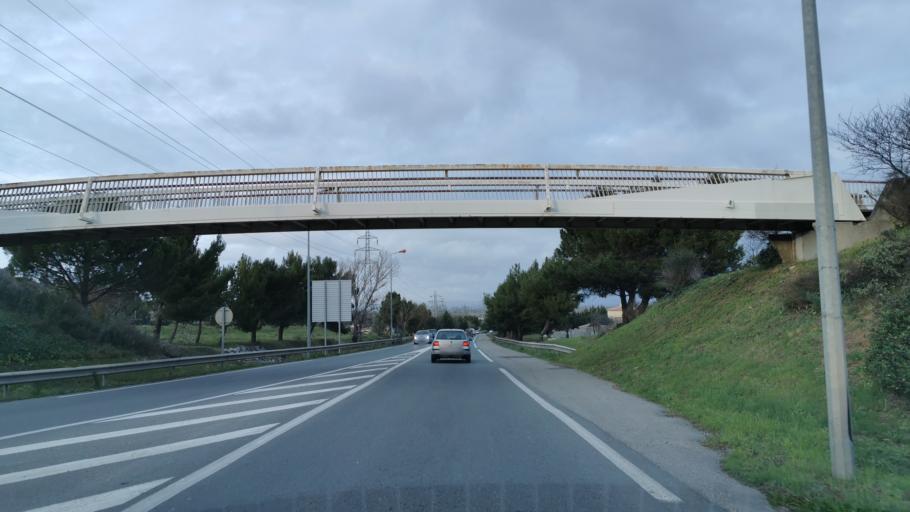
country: FR
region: Languedoc-Roussillon
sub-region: Departement de l'Aude
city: Narbonne
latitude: 43.1873
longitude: 2.9732
